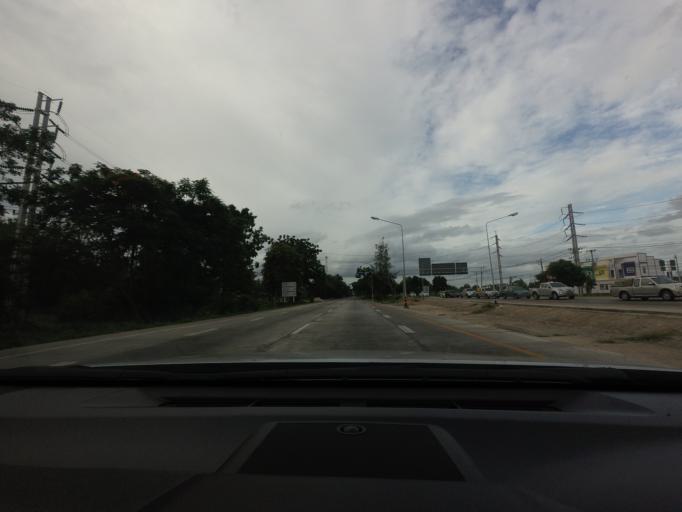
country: TH
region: Phetchaburi
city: Cha-am
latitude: 12.7194
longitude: 99.9205
